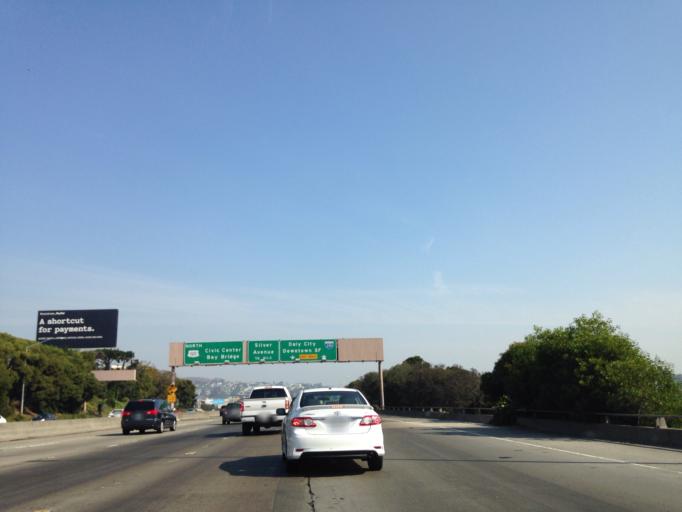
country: US
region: California
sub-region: San Mateo County
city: Brisbane
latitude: 37.7195
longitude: -122.3995
